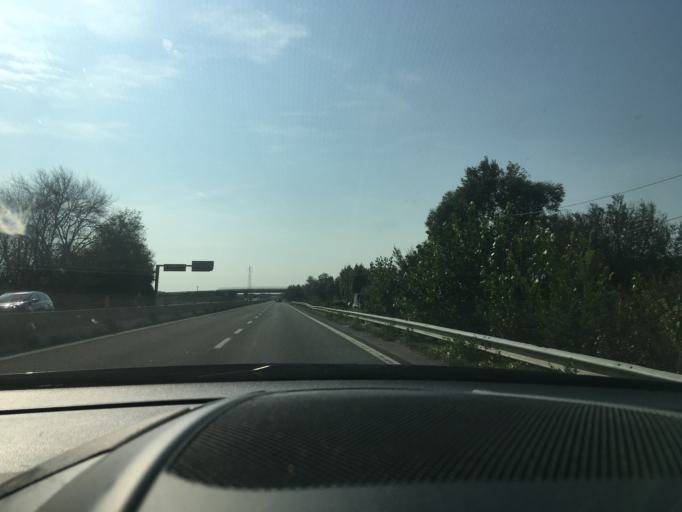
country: IT
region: Emilia-Romagna
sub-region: Provincia di Rimini
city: Bellaria-Igea Marina
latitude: 44.1392
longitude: 12.4597
